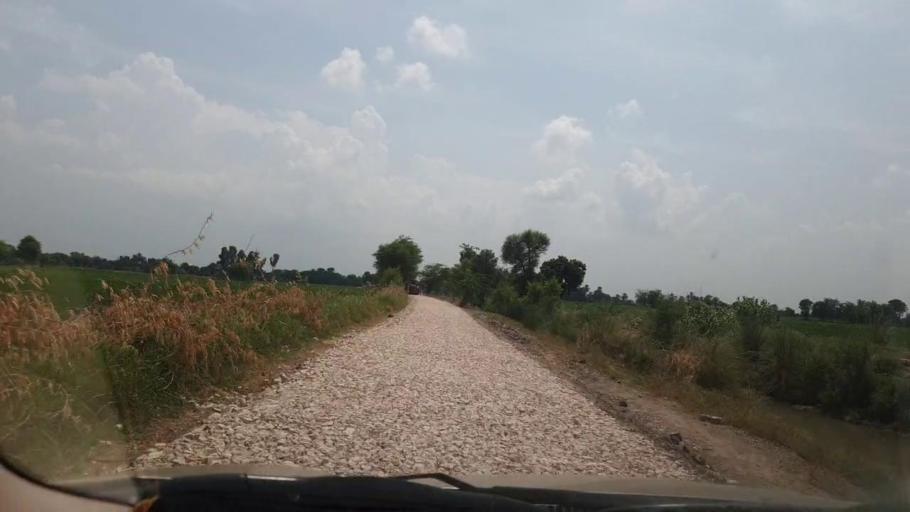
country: PK
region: Sindh
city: Larkana
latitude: 27.5670
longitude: 68.1101
